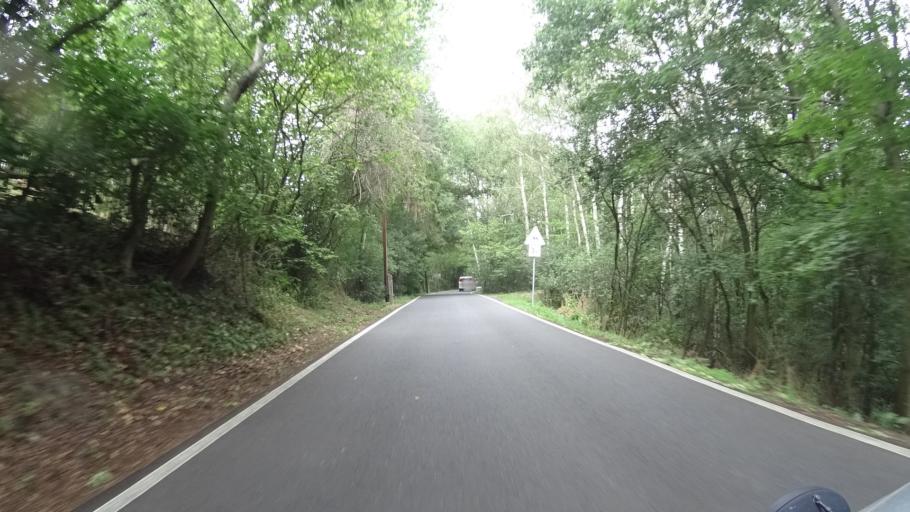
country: CZ
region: Ustecky
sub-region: Okres Litomerice
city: Litomerice
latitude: 50.5688
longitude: 14.1208
